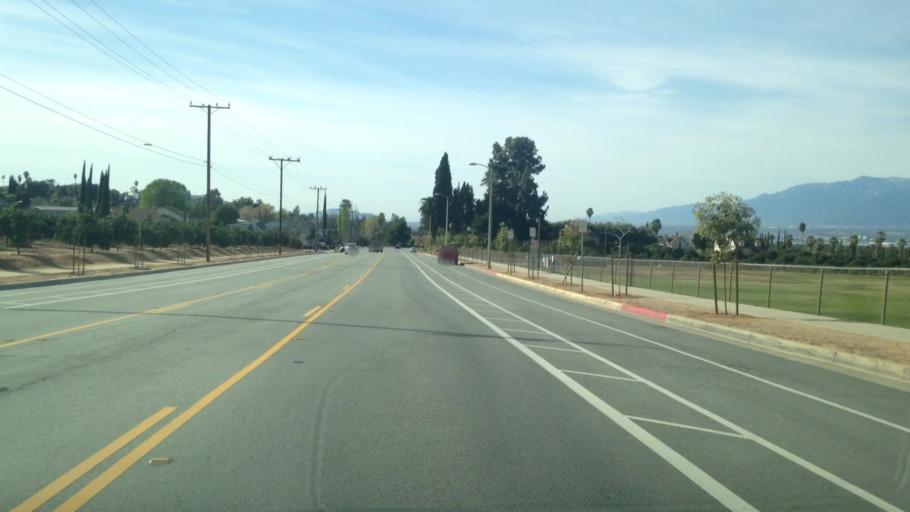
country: US
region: California
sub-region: San Bernardino County
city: Mentone
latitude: 34.0484
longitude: -117.1497
